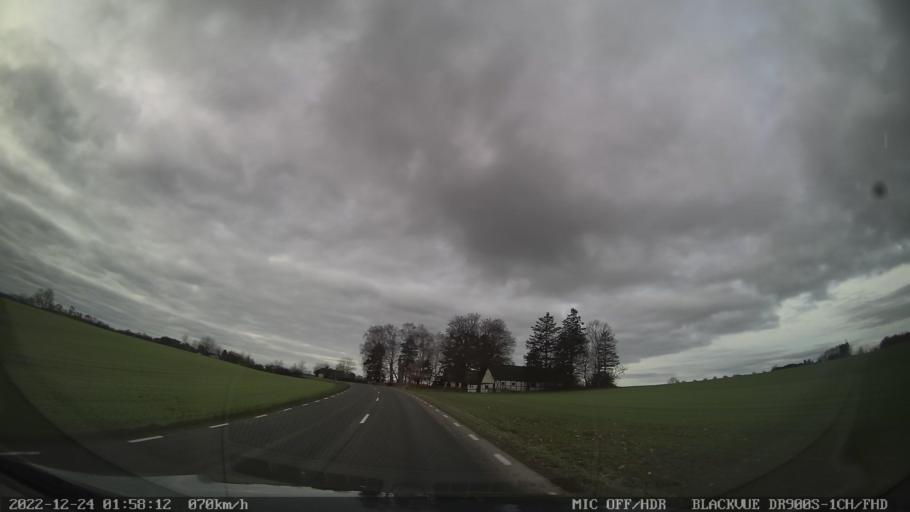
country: SE
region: Skane
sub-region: Tomelilla Kommun
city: Tomelilla
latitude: 55.6029
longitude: 14.0369
